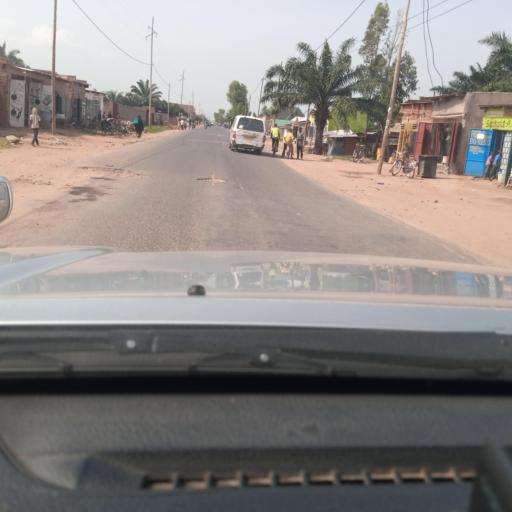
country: BI
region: Bujumbura Mairie
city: Bujumbura
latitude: -3.4543
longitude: 29.3516
